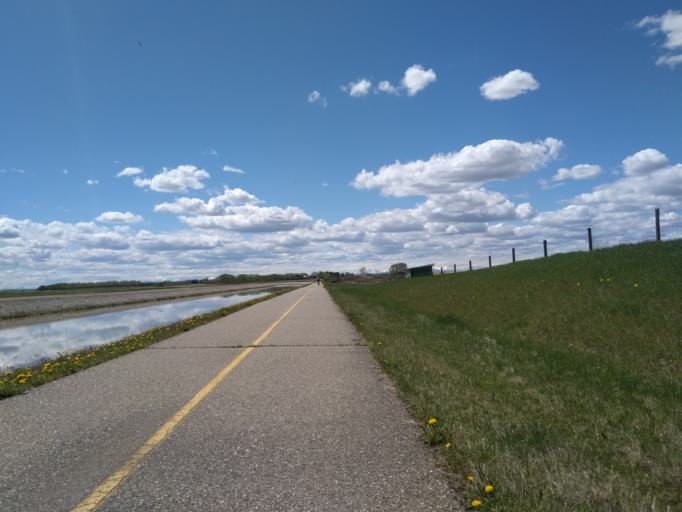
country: CA
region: Alberta
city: Chestermere
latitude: 51.0058
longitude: -113.8505
